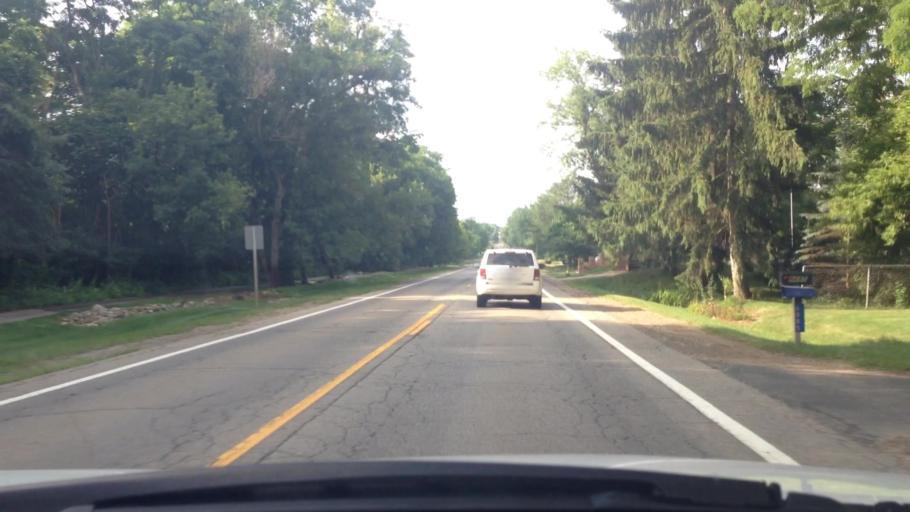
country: US
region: Michigan
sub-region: Oakland County
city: Clarkston
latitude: 42.7409
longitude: -83.3503
